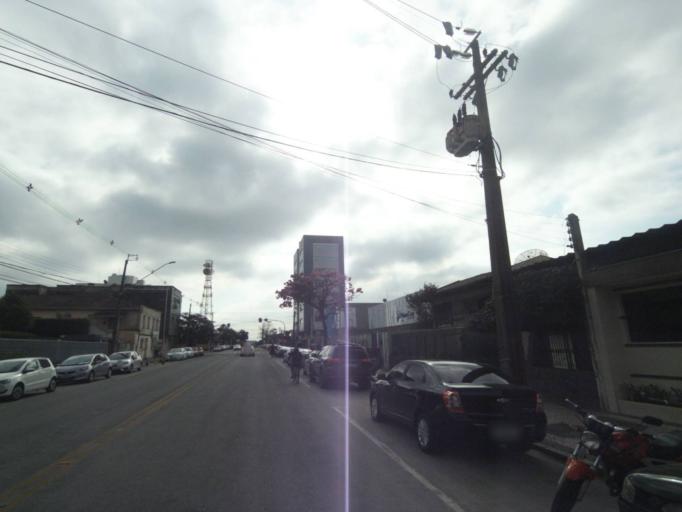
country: BR
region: Parana
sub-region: Paranagua
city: Paranagua
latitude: -25.5165
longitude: -48.5100
